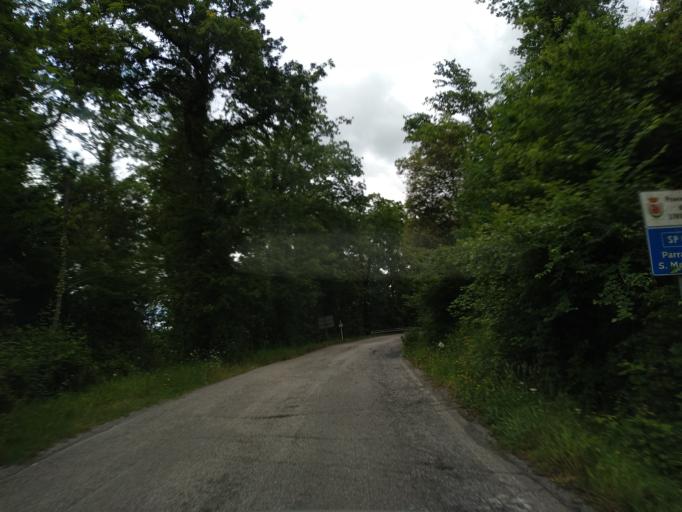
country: IT
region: Tuscany
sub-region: Provincia di Livorno
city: Guasticce
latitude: 43.5683
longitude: 10.4194
